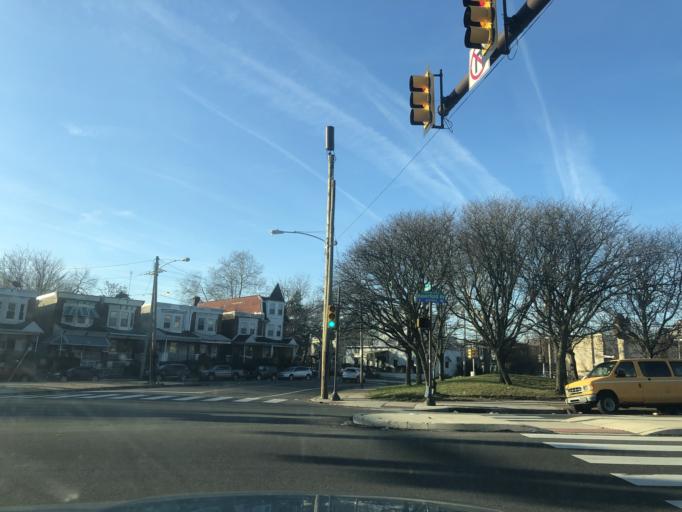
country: US
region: Pennsylvania
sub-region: Delaware County
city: Millbourne
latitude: 39.9654
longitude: -75.2255
